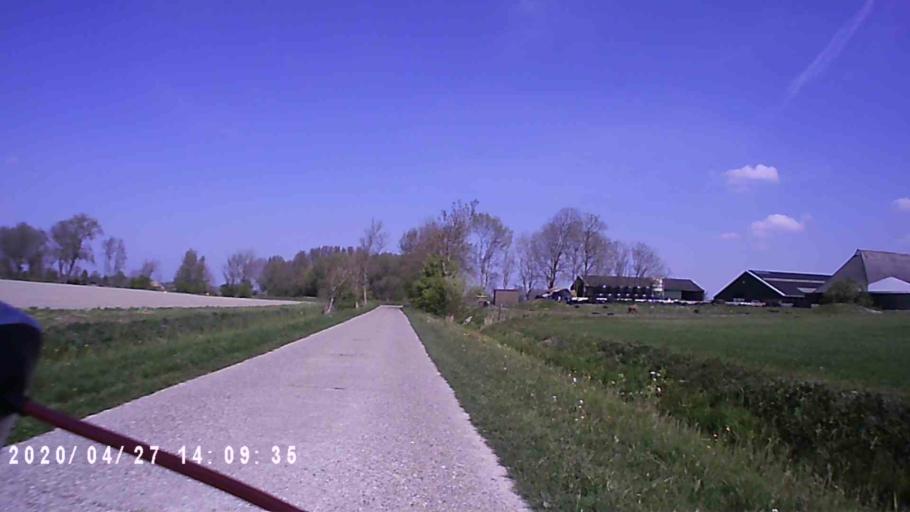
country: NL
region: Groningen
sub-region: Gemeente Zuidhorn
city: Oldehove
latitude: 53.3481
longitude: 6.3917
